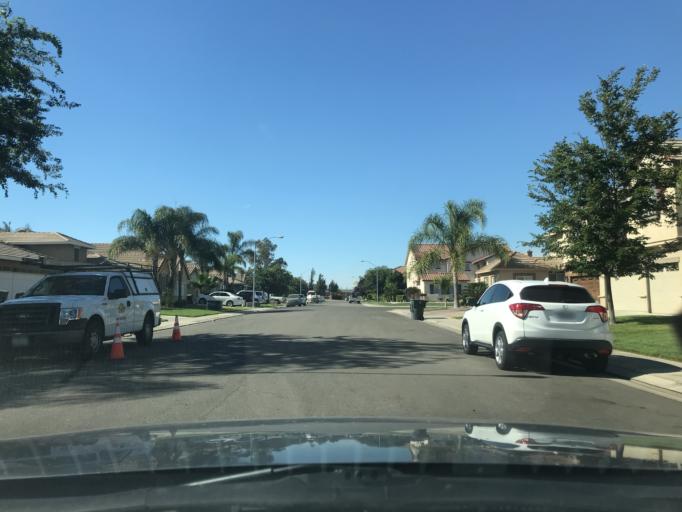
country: US
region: California
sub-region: Merced County
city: Atwater
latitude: 37.3432
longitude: -120.5742
